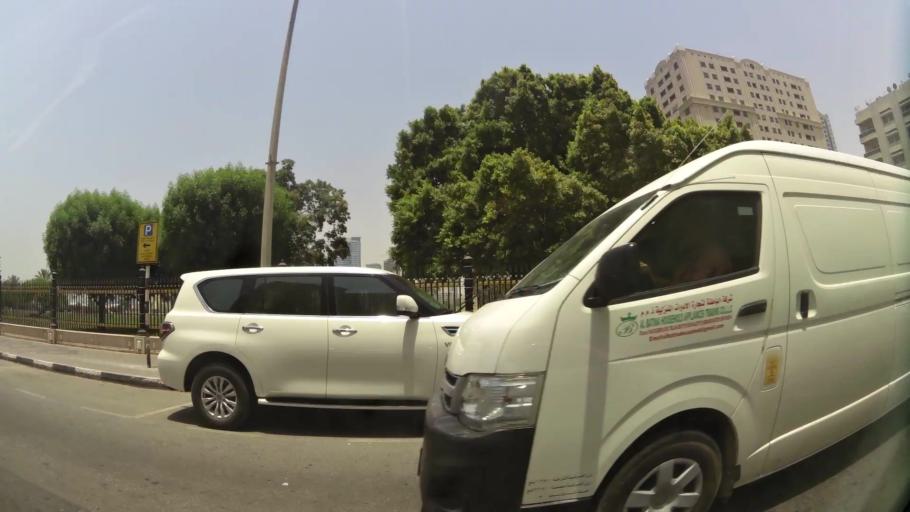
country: AE
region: Ash Shariqah
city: Sharjah
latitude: 25.3228
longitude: 55.3872
